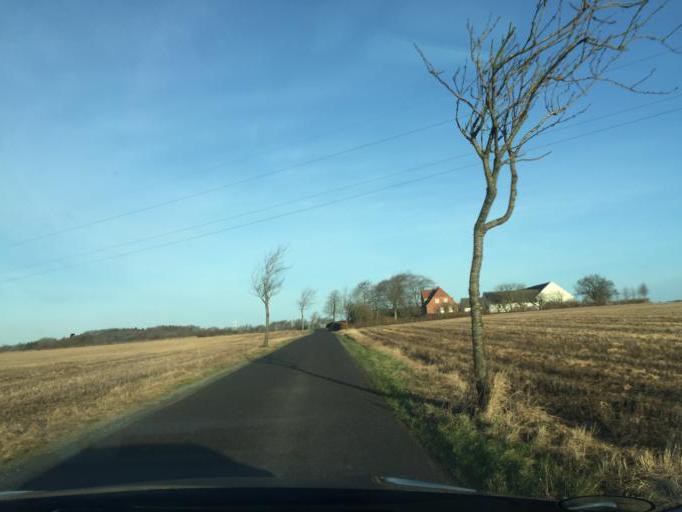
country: DK
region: South Denmark
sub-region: Middelfart Kommune
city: Ejby
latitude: 55.4543
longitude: 9.9282
